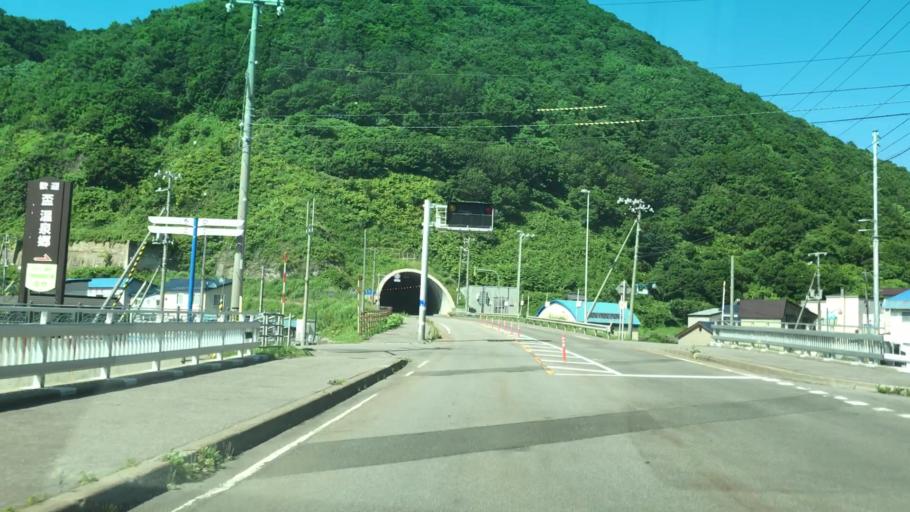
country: JP
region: Hokkaido
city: Iwanai
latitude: 43.1124
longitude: 140.4507
